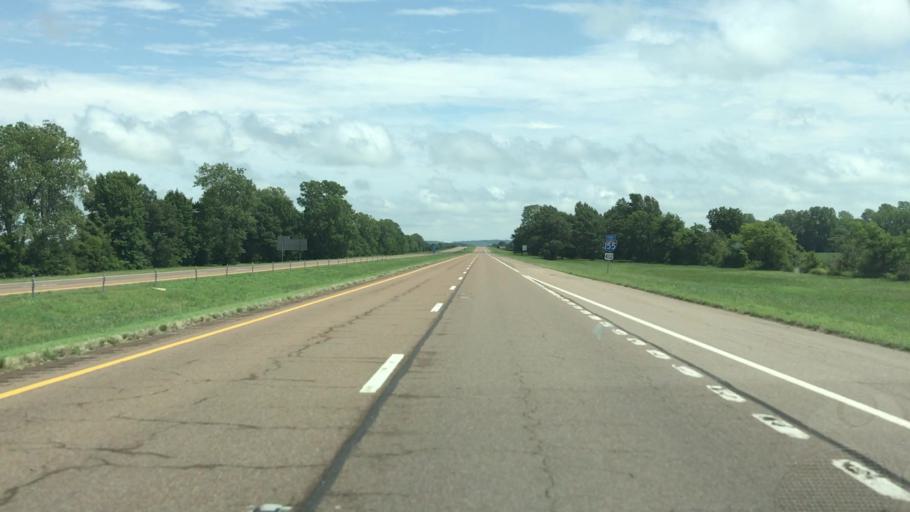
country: US
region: Missouri
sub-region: Pemiscot County
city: Caruthersville
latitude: 36.0918
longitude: -89.5804
